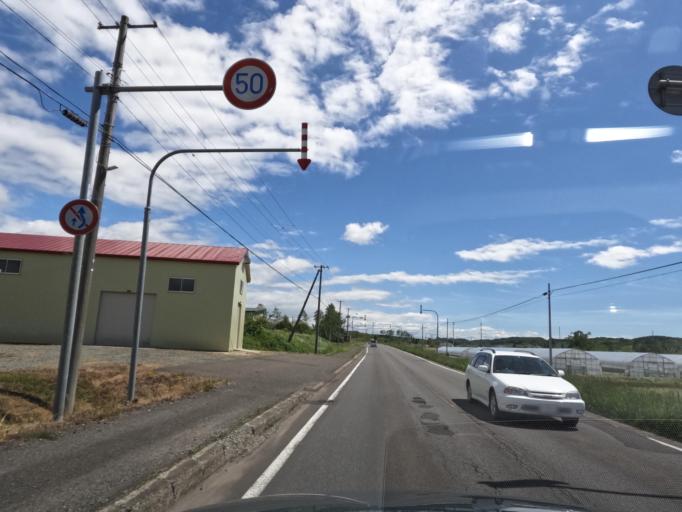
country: JP
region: Hokkaido
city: Iwamizawa
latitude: 43.1378
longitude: 141.8058
